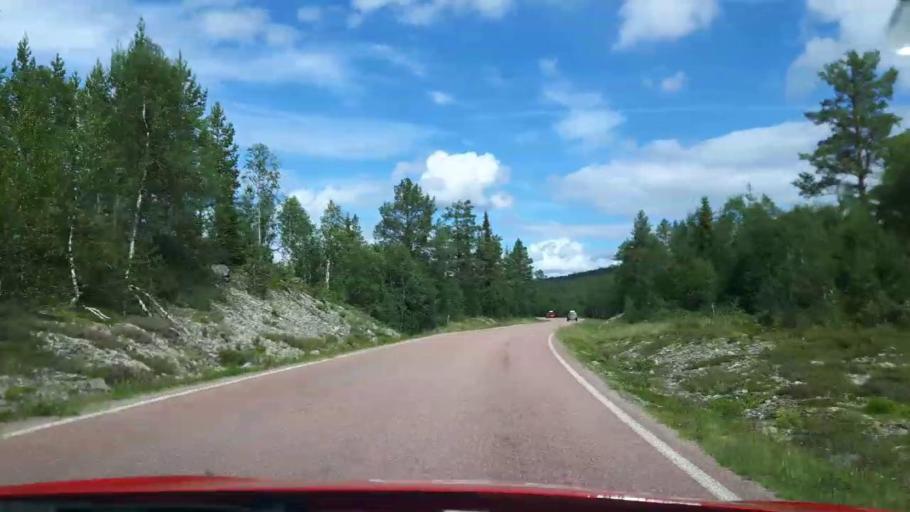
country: NO
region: Hedmark
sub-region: Trysil
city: Innbygda
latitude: 62.0136
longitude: 12.9763
